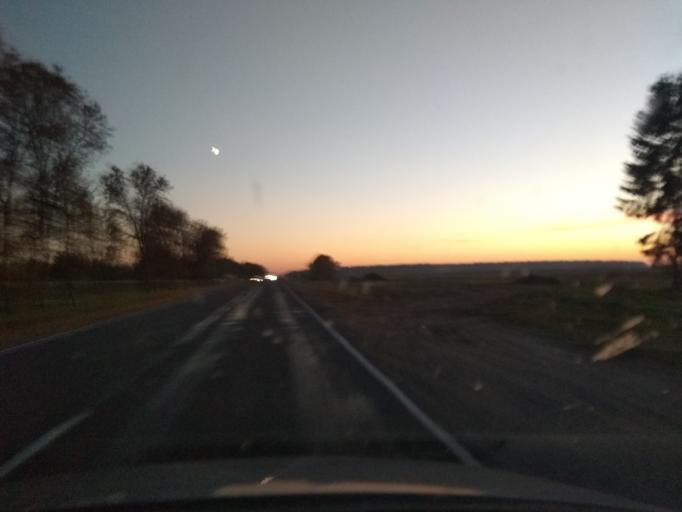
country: BY
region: Minsk
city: Dzyarzhynsk
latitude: 53.6532
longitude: 27.0757
